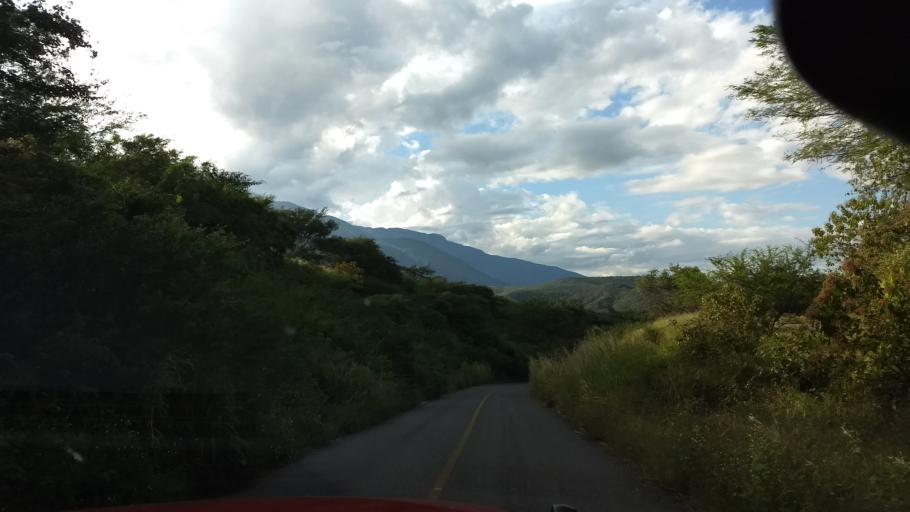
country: MX
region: Colima
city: Suchitlan
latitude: 19.4501
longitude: -103.8189
